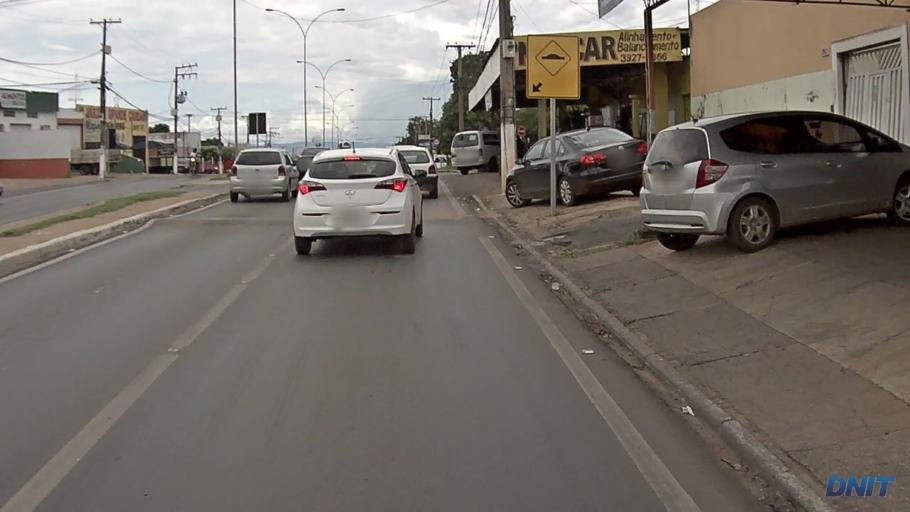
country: BR
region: Mato Grosso
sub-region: Varzea Grande
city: Varzea Grande
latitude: -15.6456
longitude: -56.1400
